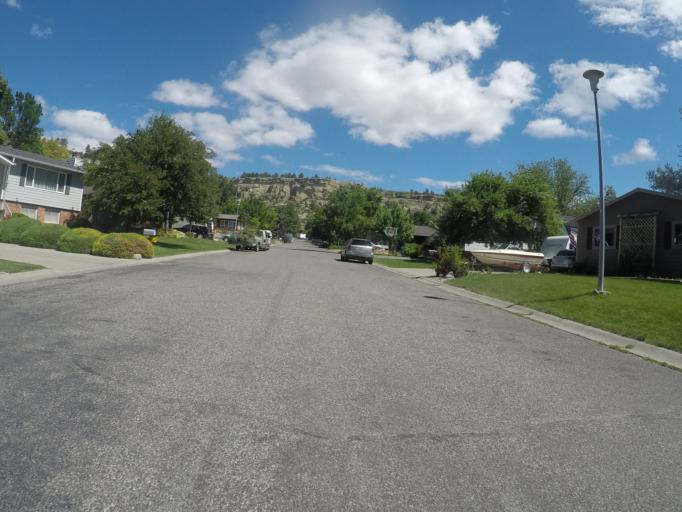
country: US
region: Montana
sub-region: Yellowstone County
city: Billings
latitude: 45.7995
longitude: -108.5664
